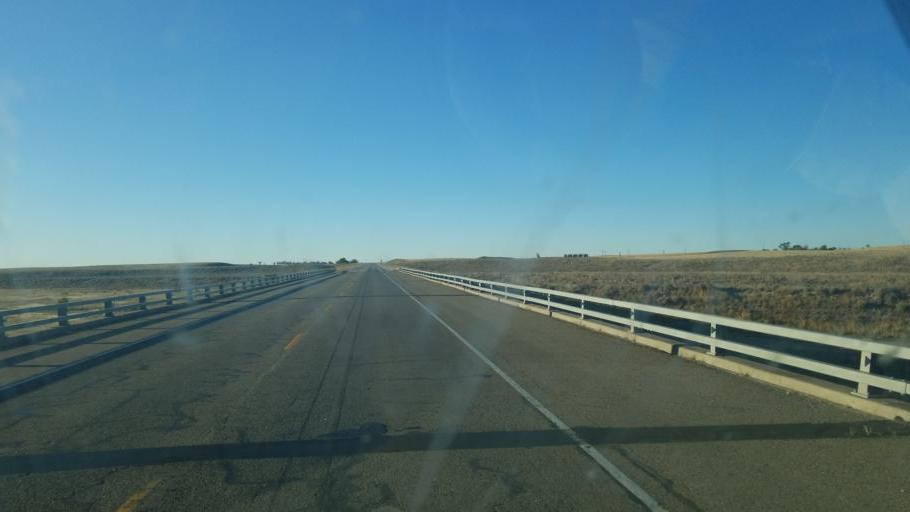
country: US
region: Colorado
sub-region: Kiowa County
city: Eads
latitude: 38.7418
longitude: -102.7766
